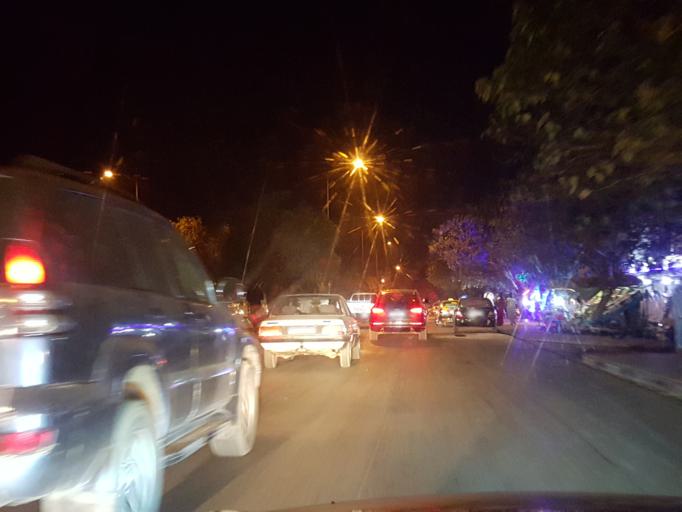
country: SN
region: Dakar
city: Grand Dakar
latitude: 14.7330
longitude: -17.4604
